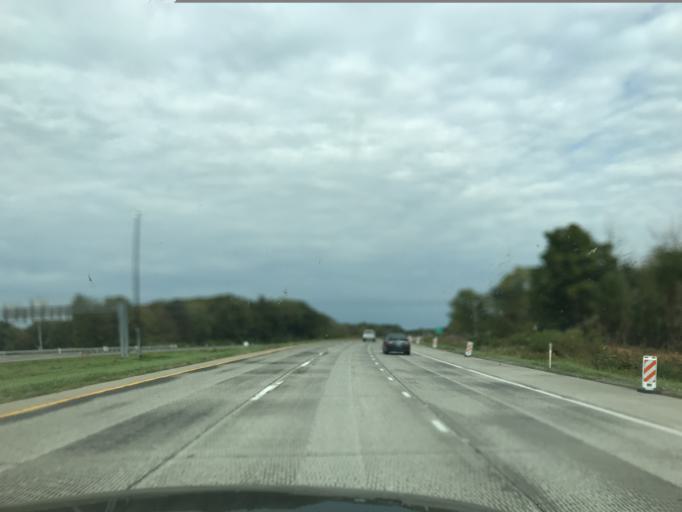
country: US
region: Pennsylvania
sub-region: Erie County
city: Erie
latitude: 42.0378
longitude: -80.1217
